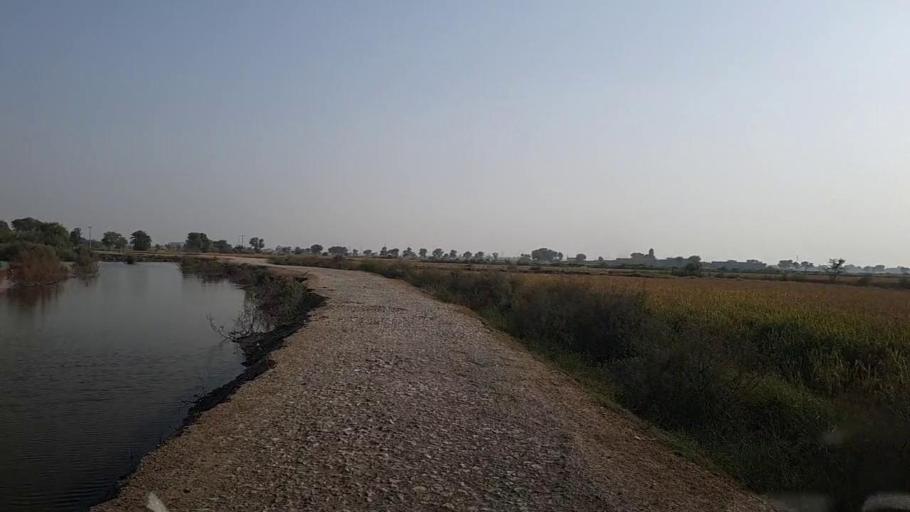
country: PK
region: Sindh
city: Kandhkot
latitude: 28.2889
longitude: 69.2567
